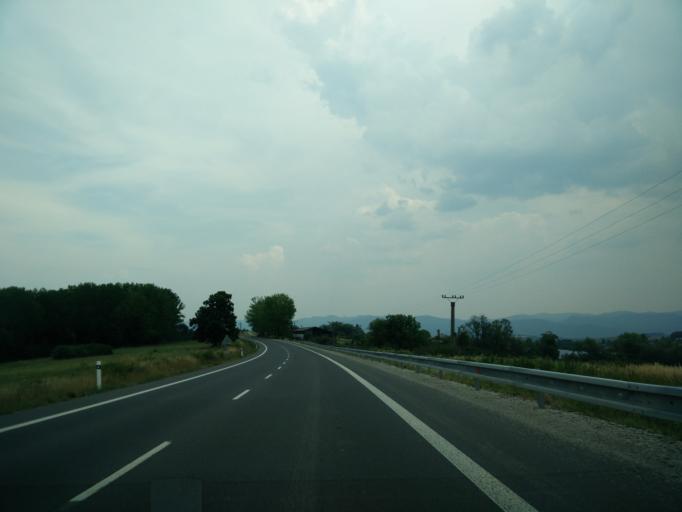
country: SK
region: Banskobystricky
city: Ziar nad Hronom
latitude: 48.6279
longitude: 18.7828
